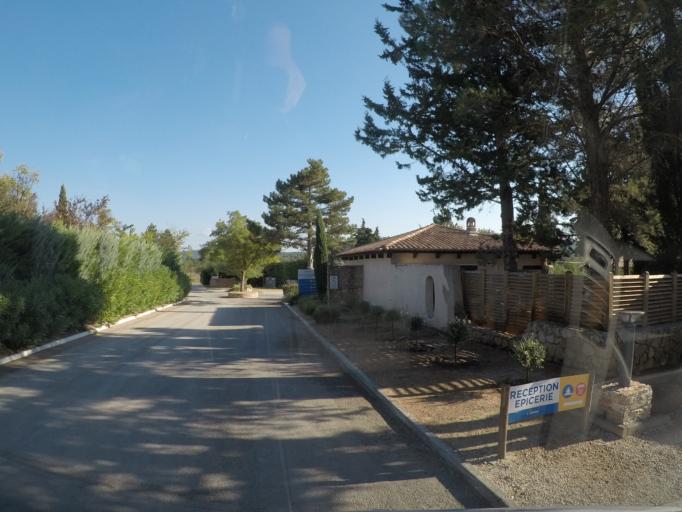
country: FR
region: Provence-Alpes-Cote d'Azur
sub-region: Departement du Vaucluse
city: Lourmarin
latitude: 43.7683
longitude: 5.3724
